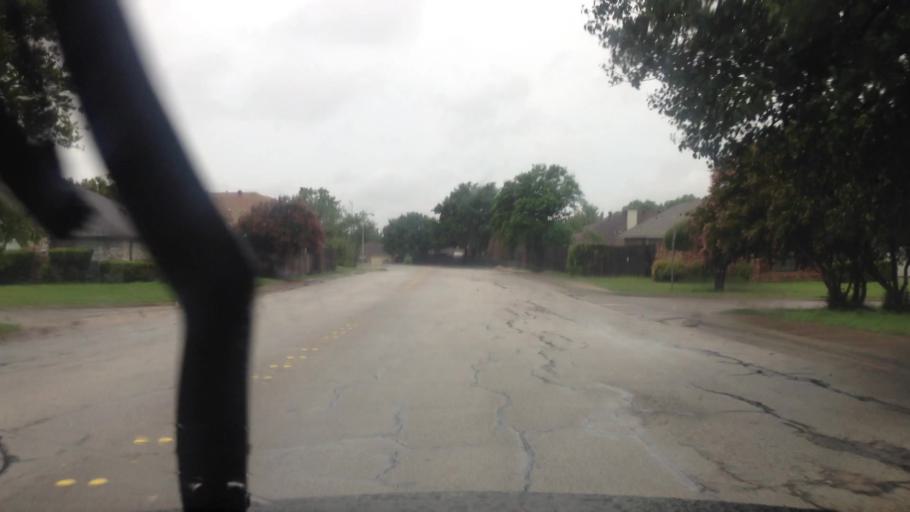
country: US
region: Texas
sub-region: Tarrant County
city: North Richland Hills
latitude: 32.8670
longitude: -97.2194
